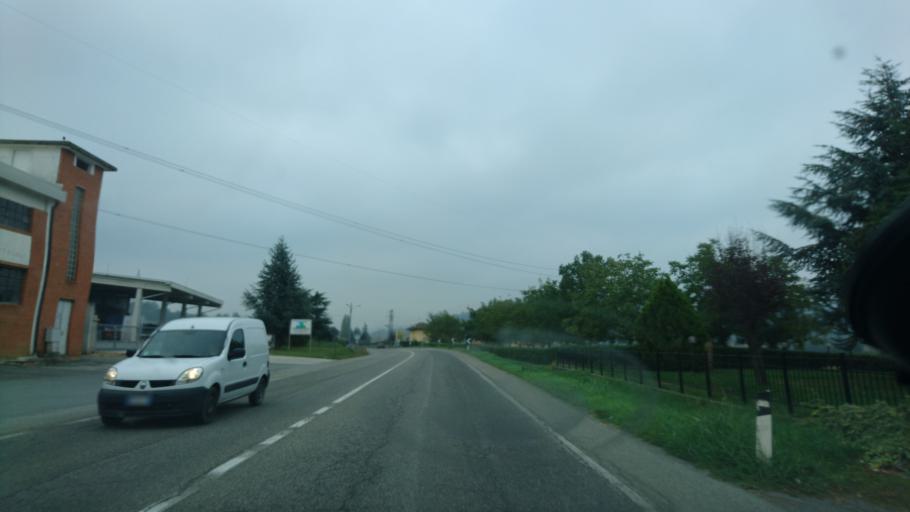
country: IT
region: Piedmont
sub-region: Provincia di Alessandria
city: Bistagno
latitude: 44.6584
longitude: 8.3776
